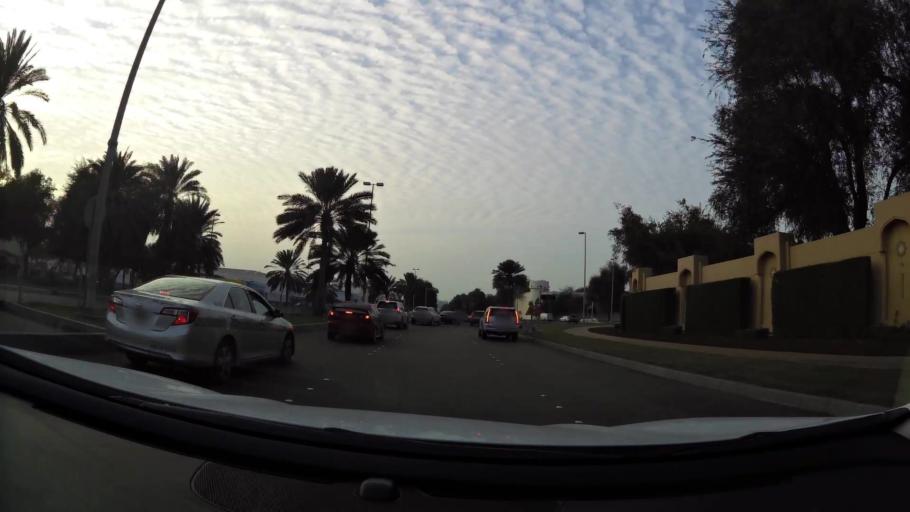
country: AE
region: Abu Dhabi
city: Abu Dhabi
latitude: 24.4523
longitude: 54.3651
